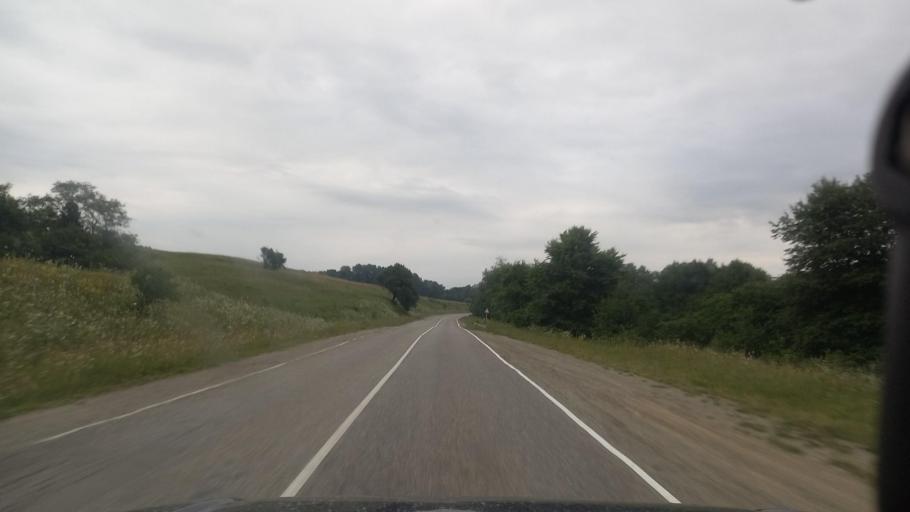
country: RU
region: Karachayevo-Cherkesiya
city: Mednogorskiy
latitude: 43.9421
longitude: 41.1259
